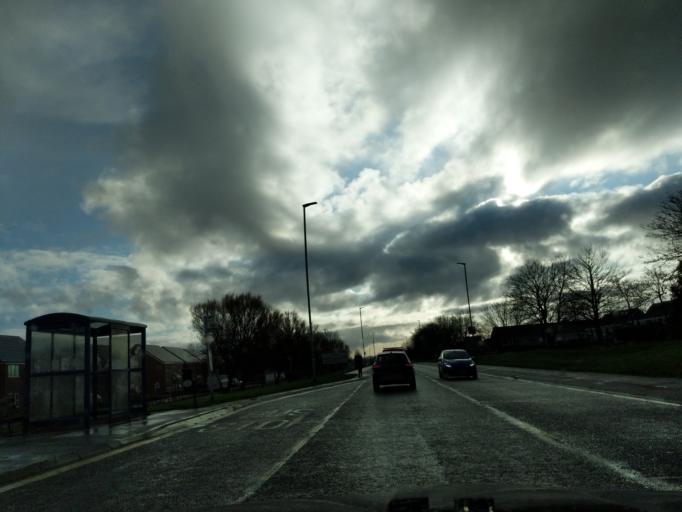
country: GB
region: England
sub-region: Northumberland
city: Blyth
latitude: 55.1143
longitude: -1.5063
